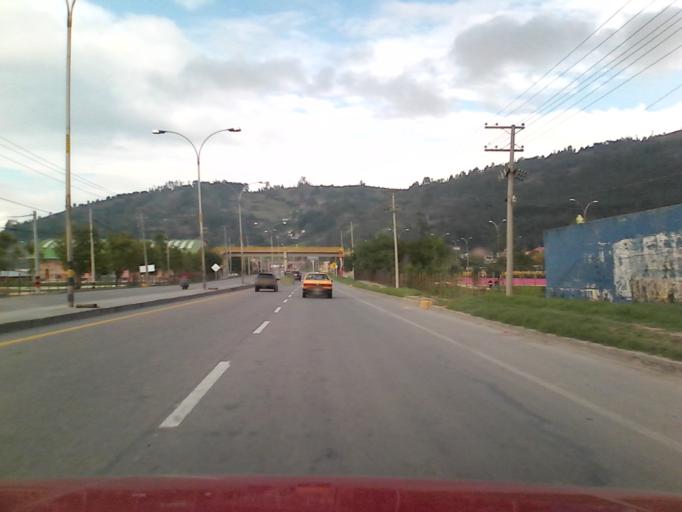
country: CO
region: Boyaca
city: Duitama
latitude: 5.8059
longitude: -73.0335
